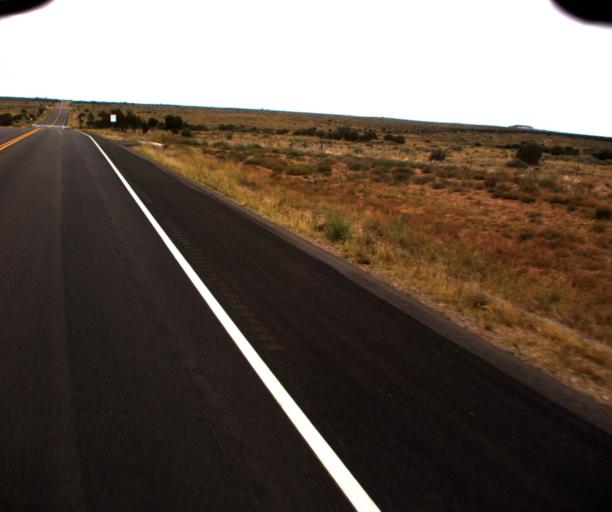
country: US
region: Arizona
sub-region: Navajo County
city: Snowflake
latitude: 34.5955
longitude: -110.0873
